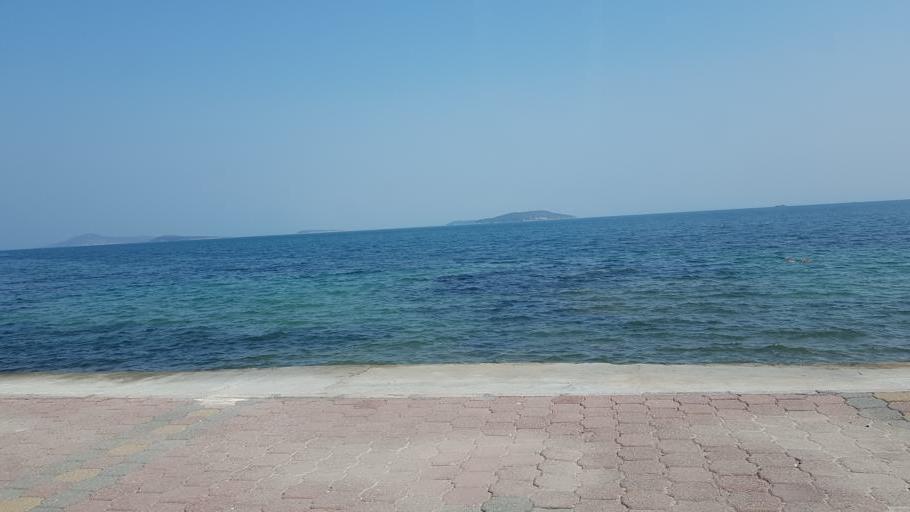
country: TR
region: Izmir
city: Urla
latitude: 38.3677
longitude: 26.7650
